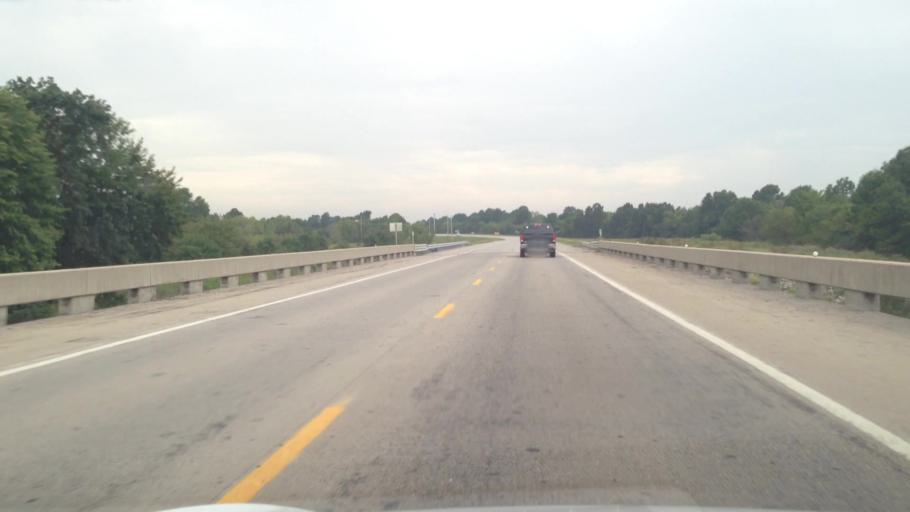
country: US
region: Kansas
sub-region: Cherokee County
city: Baxter Springs
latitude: 37.0629
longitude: -94.7296
